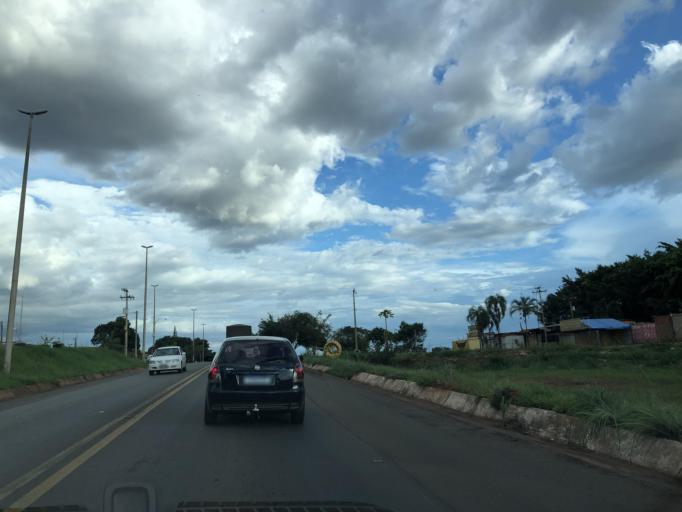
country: BR
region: Goias
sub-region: Luziania
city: Luziania
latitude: -16.0400
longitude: -48.0638
